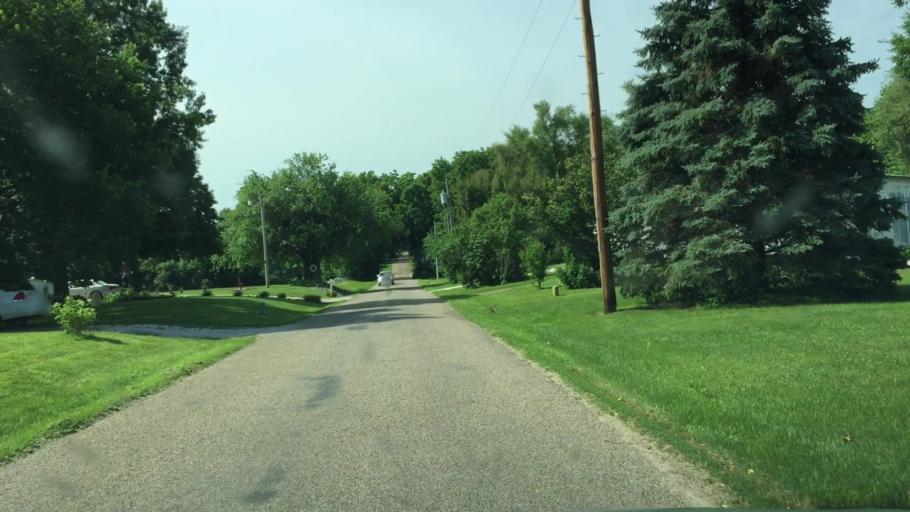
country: US
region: Illinois
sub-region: Hancock County
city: Nauvoo
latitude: 40.5482
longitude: -91.3754
